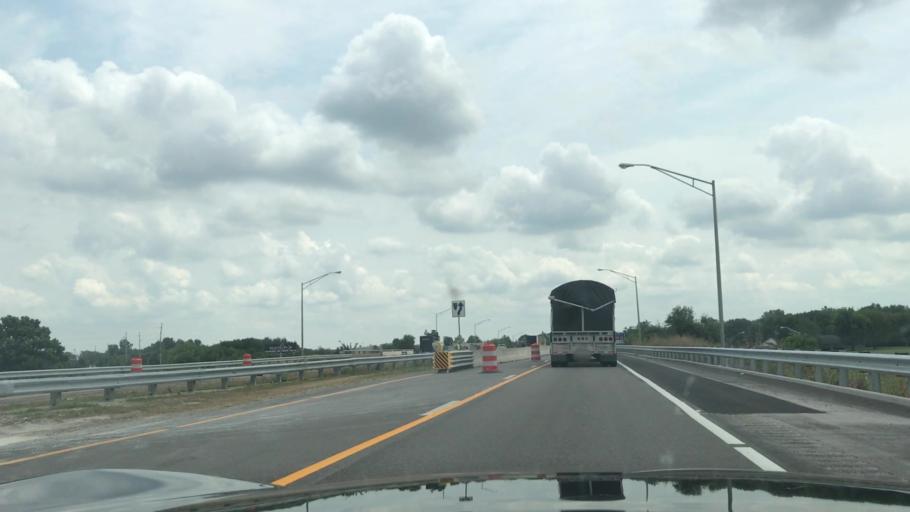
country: US
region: Kentucky
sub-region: Warren County
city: Bowling Green
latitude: 36.9585
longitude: -86.4974
